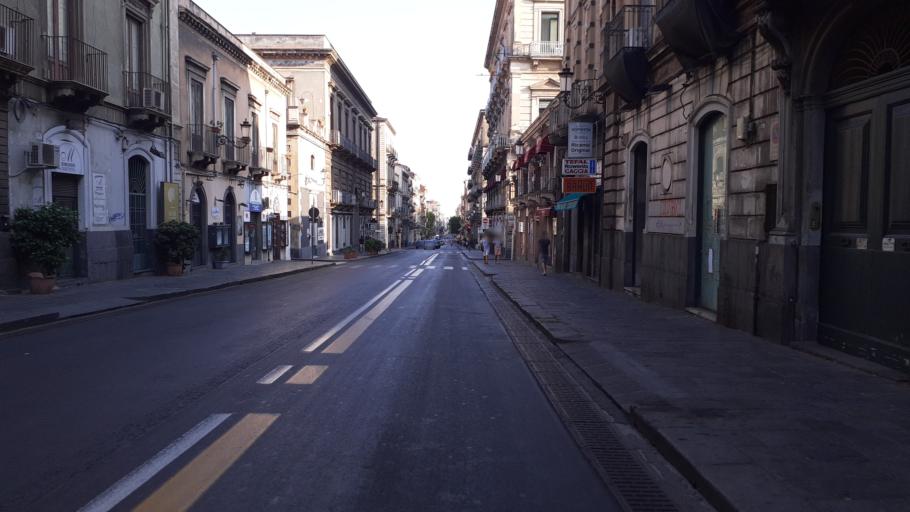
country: IT
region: Sicily
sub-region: Catania
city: Catania
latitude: 37.5141
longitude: 15.0846
